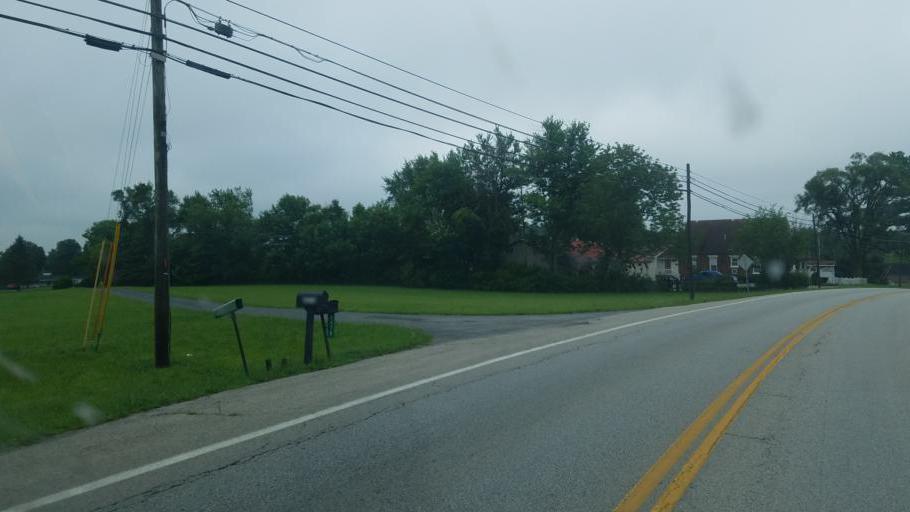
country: US
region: Ohio
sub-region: Highland County
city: Hillsboro
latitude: 39.2437
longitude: -83.6053
